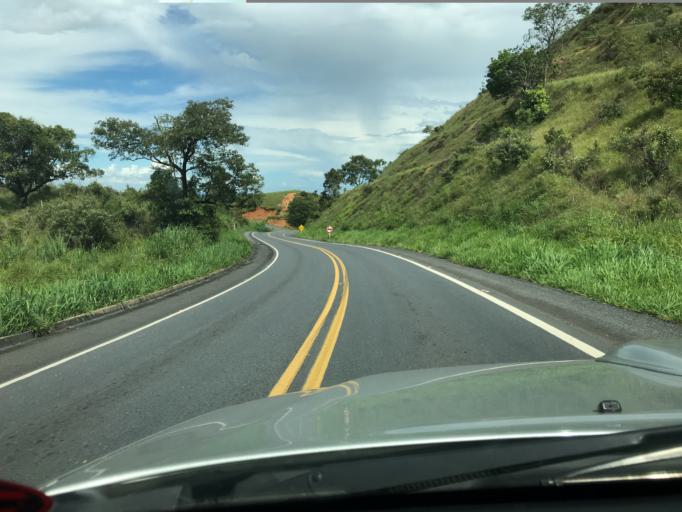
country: BR
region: Minas Gerais
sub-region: Campos Altos
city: Campos Altos
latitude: -19.7921
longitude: -46.0396
